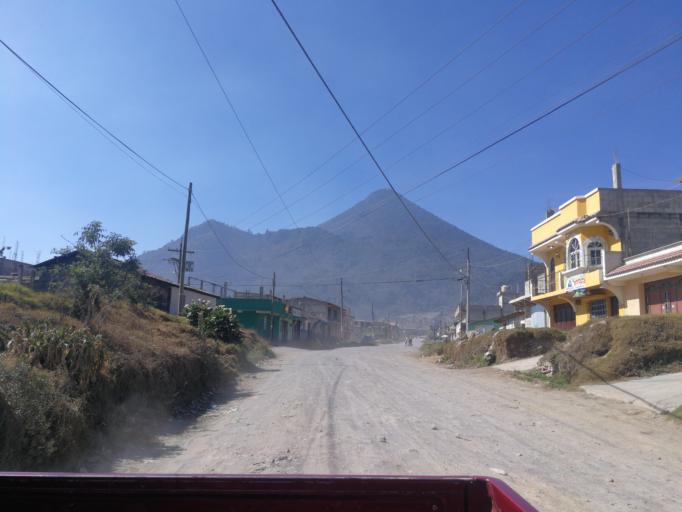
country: GT
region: Quetzaltenango
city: Quetzaltenango
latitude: 14.7960
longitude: -91.5464
